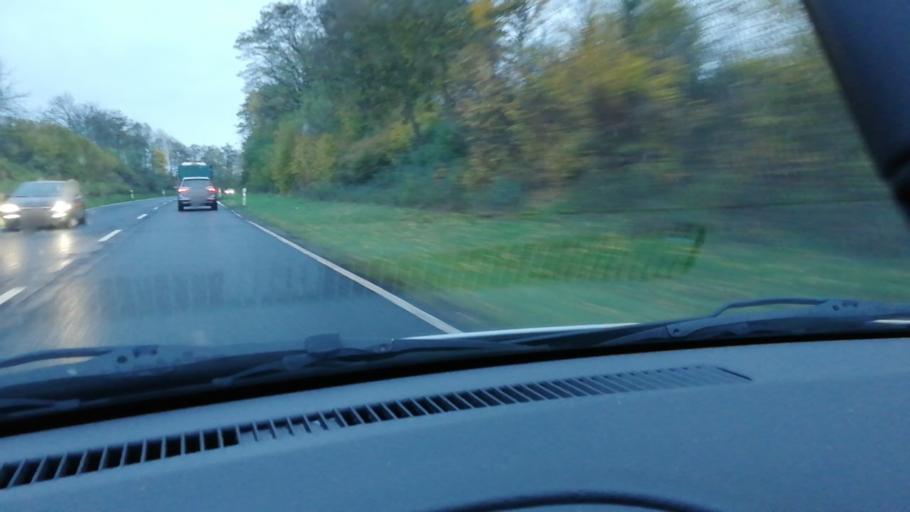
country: DE
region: Bavaria
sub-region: Regierungsbezirk Unterfranken
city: Hosbach
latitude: 50.0239
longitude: 9.2120
